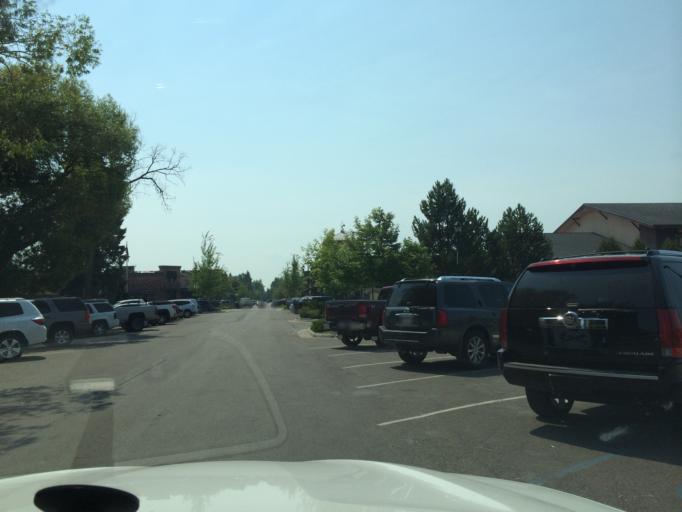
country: US
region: Montana
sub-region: Flathead County
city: Whitefish
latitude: 48.4133
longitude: -114.3368
